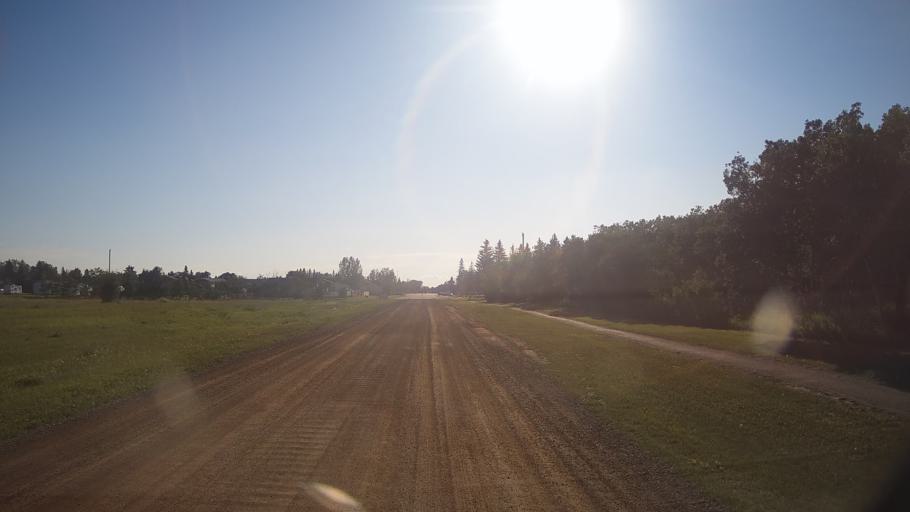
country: CA
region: Saskatchewan
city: Lanigan
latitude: 51.8507
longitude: -105.0198
